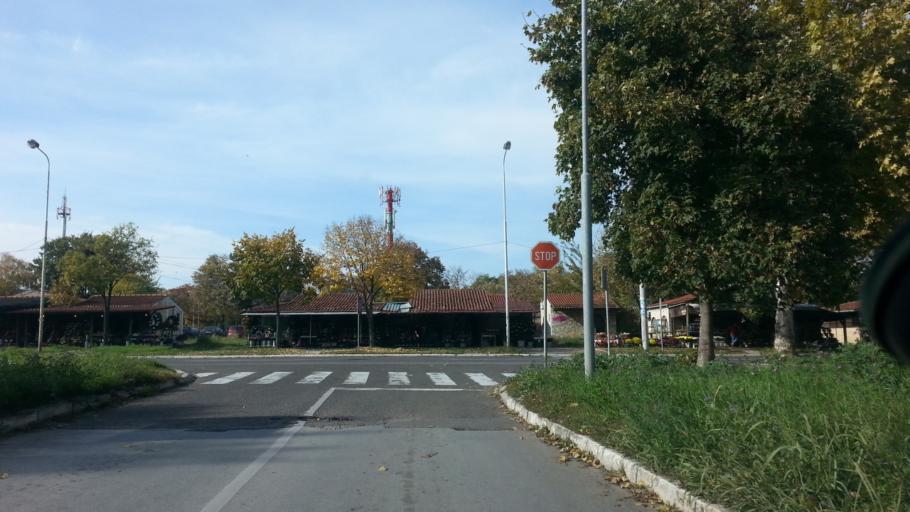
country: RS
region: Central Serbia
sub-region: Belgrade
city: Zemun
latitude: 44.8169
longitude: 20.3713
